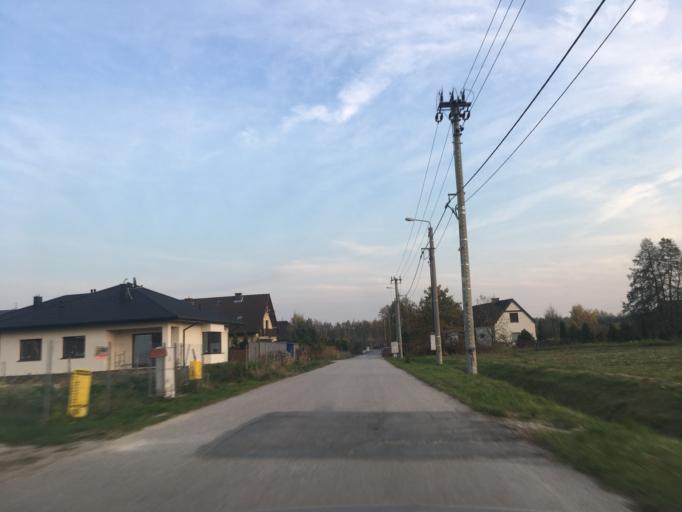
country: PL
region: Masovian Voivodeship
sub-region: Powiat piaseczynski
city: Lesznowola
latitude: 52.0487
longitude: 20.9286
